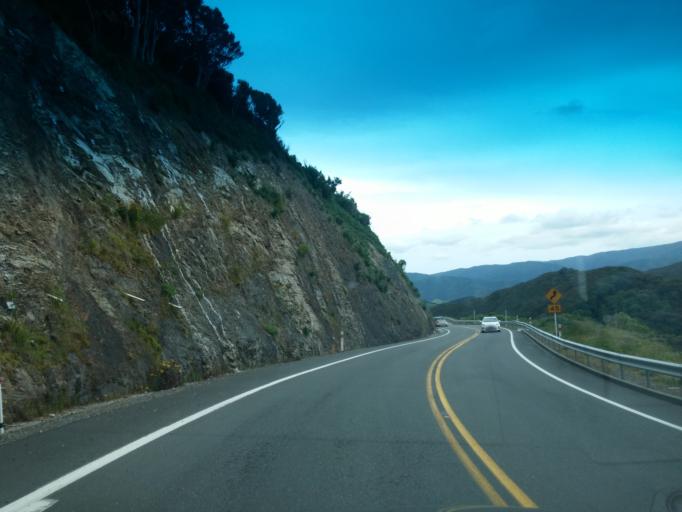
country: NZ
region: Wellington
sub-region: Upper Hutt City
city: Upper Hutt
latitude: -41.1147
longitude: 175.2227
